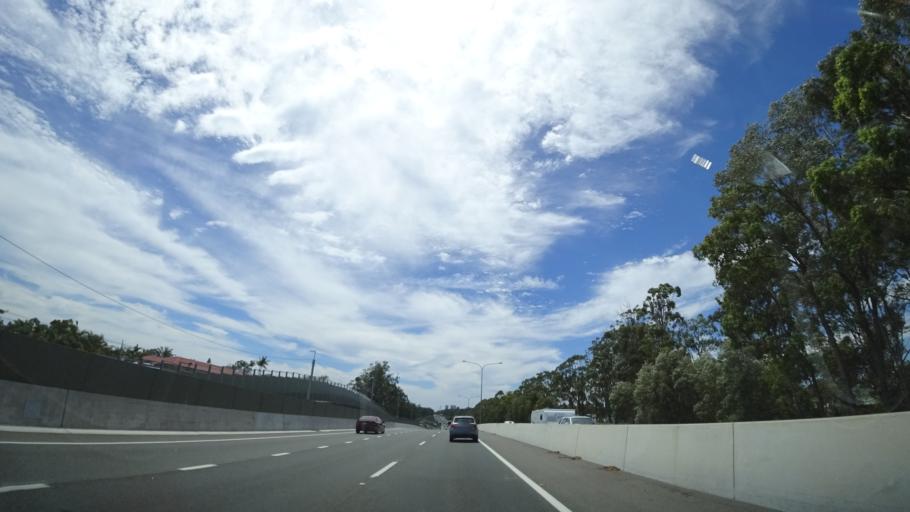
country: AU
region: Queensland
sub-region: Gold Coast
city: Southport
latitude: -27.9635
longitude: 153.3664
